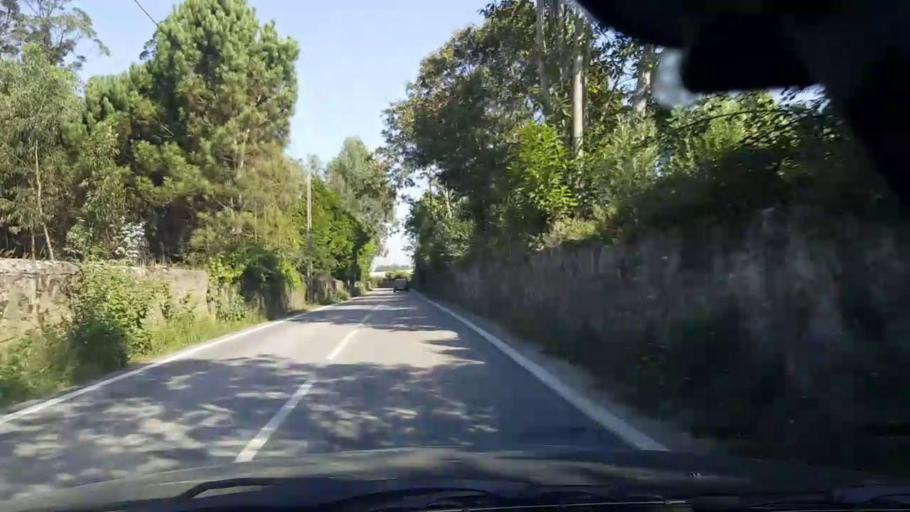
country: PT
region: Porto
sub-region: Vila do Conde
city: Arvore
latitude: 41.3194
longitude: -8.6795
